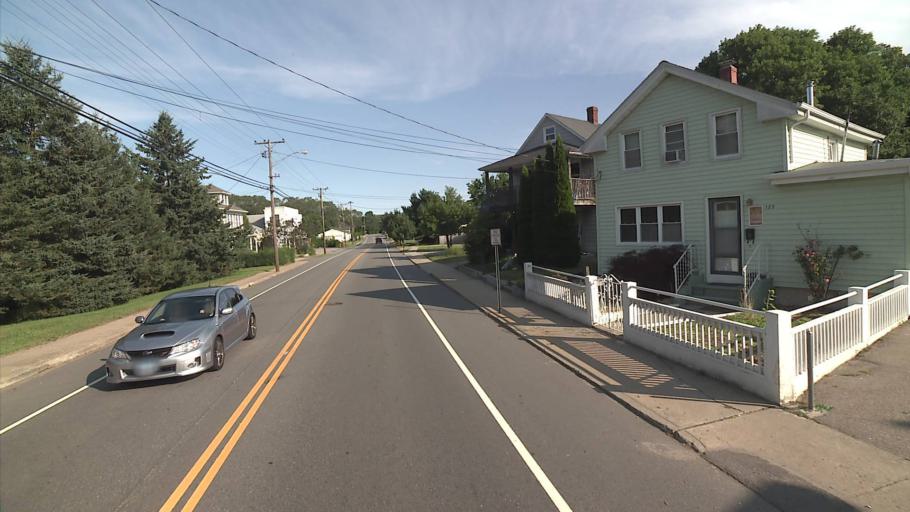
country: US
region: Connecticut
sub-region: New London County
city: Pawcatuck
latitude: 41.3828
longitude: -71.8422
